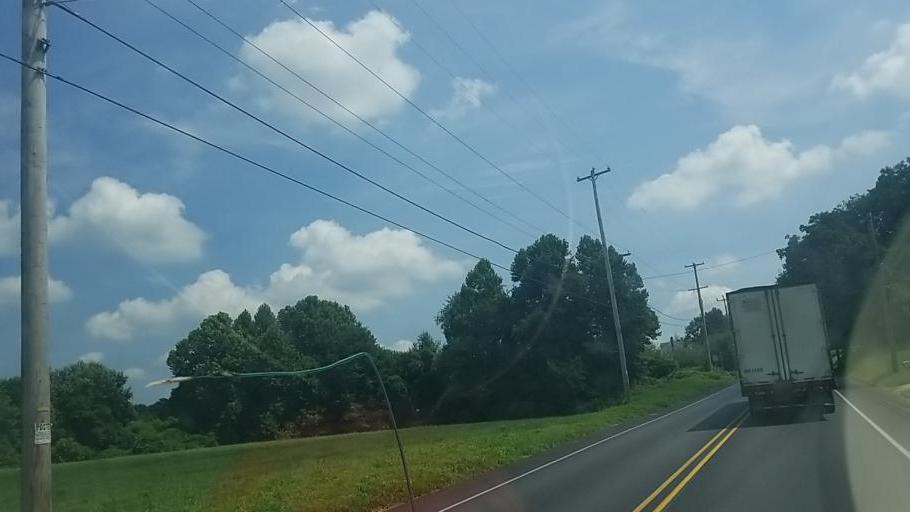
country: US
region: Pennsylvania
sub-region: Chester County
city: Avondale
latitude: 39.8195
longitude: -75.7743
